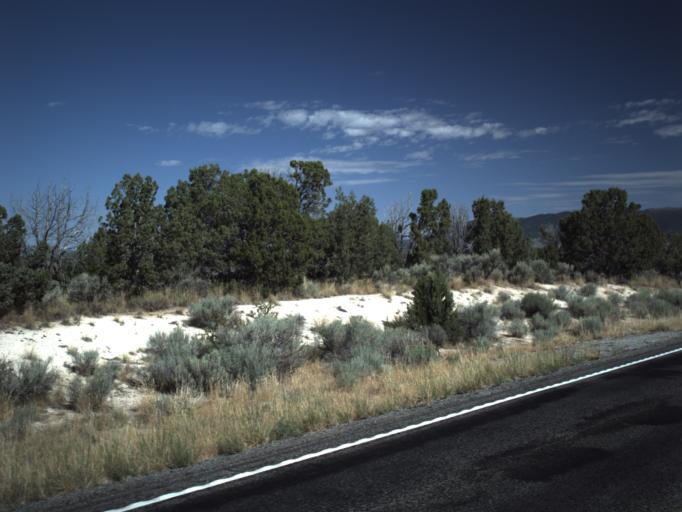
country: US
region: Utah
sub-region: Juab County
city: Mona
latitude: 39.8782
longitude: -112.1380
